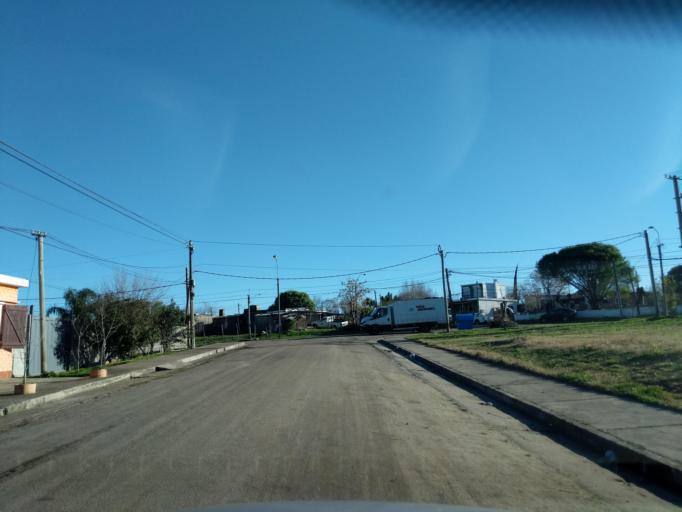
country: UY
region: Florida
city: Florida
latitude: -34.0986
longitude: -56.2388
